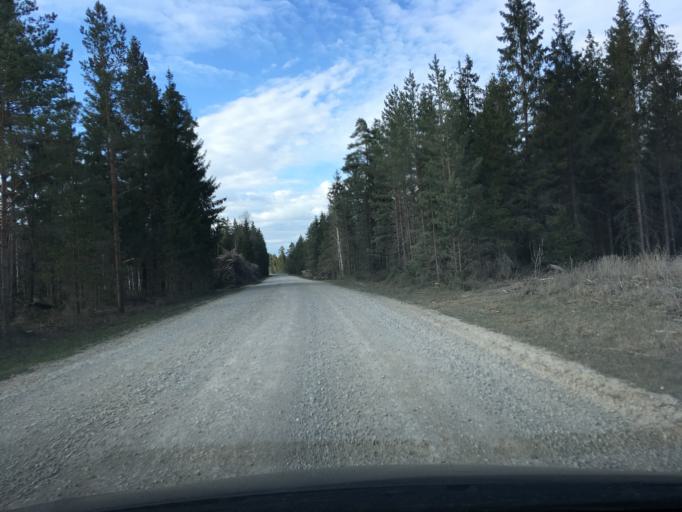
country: EE
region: Raplamaa
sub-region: Maerjamaa vald
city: Marjamaa
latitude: 58.9617
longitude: 24.3301
